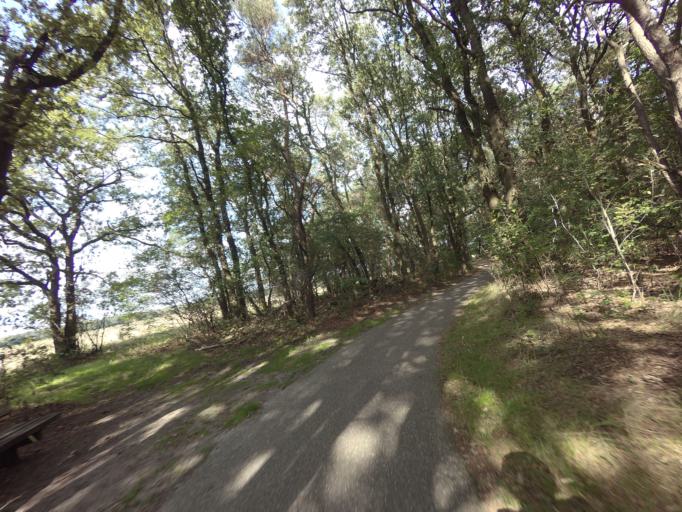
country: NL
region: Drenthe
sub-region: Gemeente De Wolden
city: Ruinen
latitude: 52.7941
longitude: 6.3523
